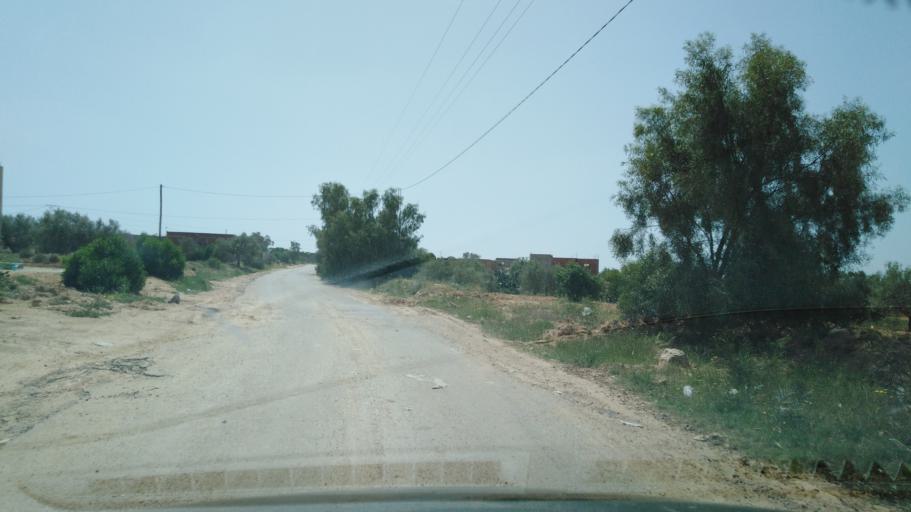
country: TN
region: Safaqis
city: Sfax
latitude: 34.7215
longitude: 10.5306
